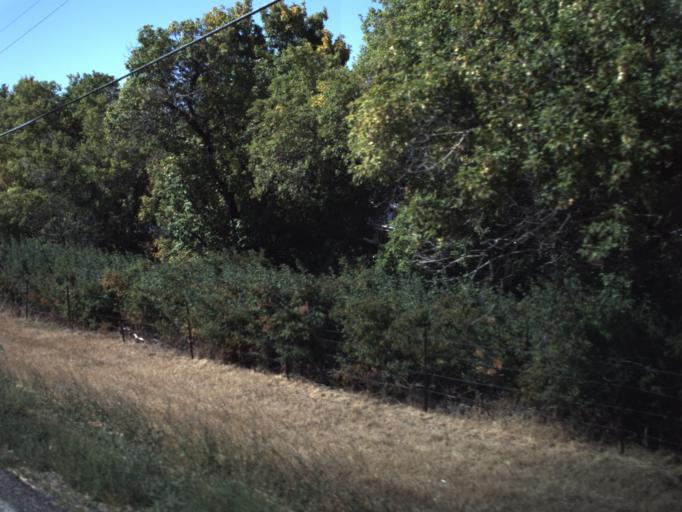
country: US
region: Utah
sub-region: Cache County
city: Hyrum
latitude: 41.5835
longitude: -111.8385
